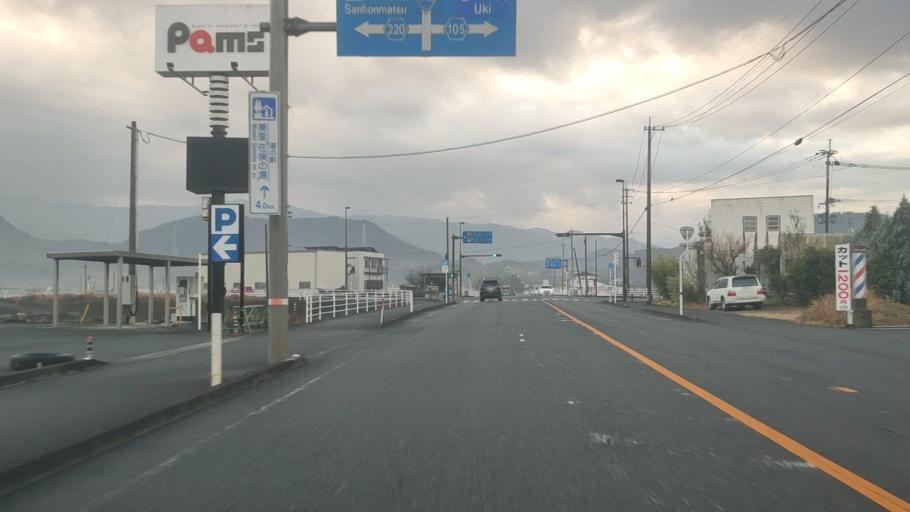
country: JP
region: Kumamoto
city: Matsubase
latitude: 32.6486
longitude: 130.8113
